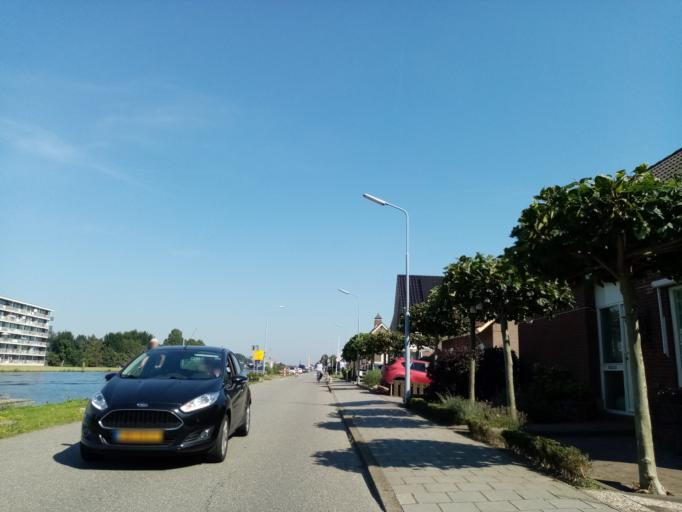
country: NL
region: South Holland
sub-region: Gemeente Lisse
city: Lisse
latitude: 52.2425
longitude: 4.5661
